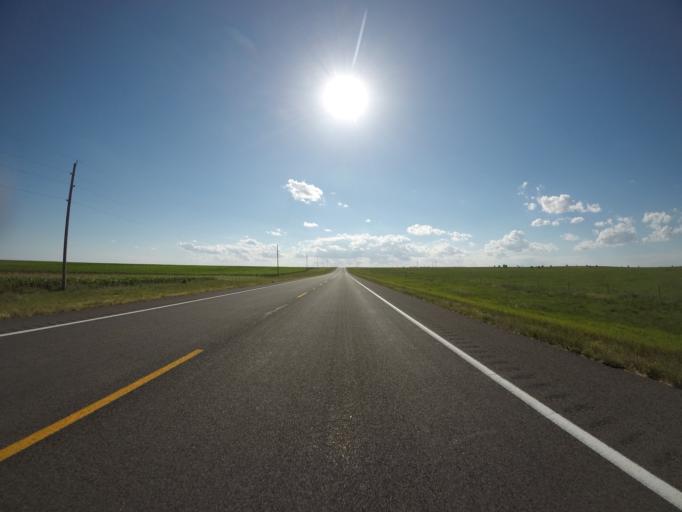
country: US
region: Colorado
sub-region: Morgan County
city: Fort Morgan
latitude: 40.6107
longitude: -103.7566
